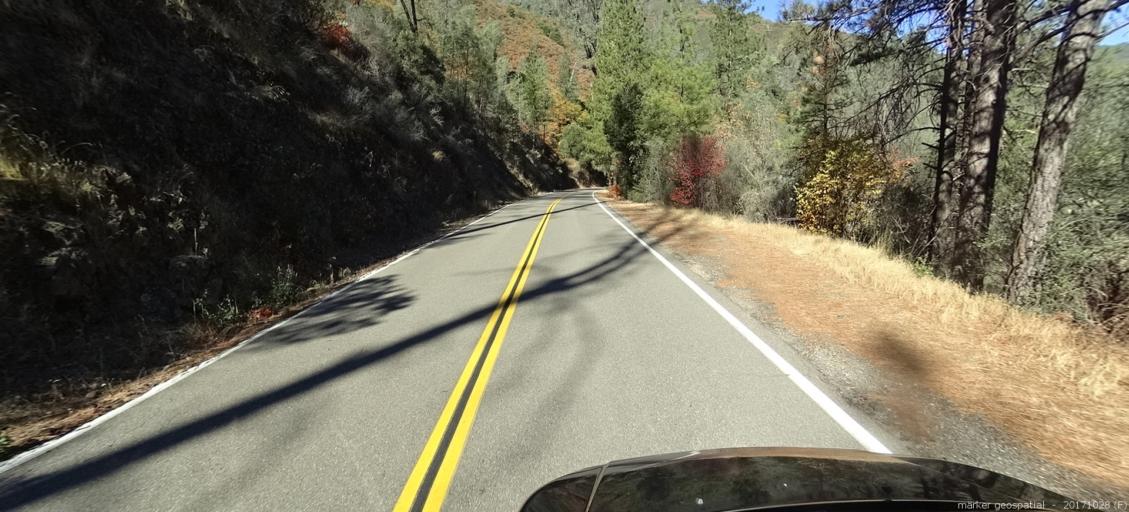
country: US
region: California
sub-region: Trinity County
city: Lewiston
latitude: 40.7299
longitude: -122.6245
